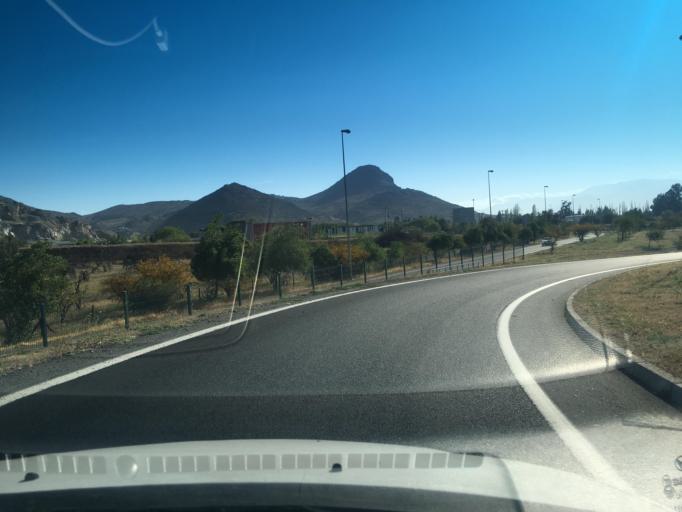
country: CL
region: Santiago Metropolitan
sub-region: Provincia de Chacabuco
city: Chicureo Abajo
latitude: -33.3021
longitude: -70.6595
